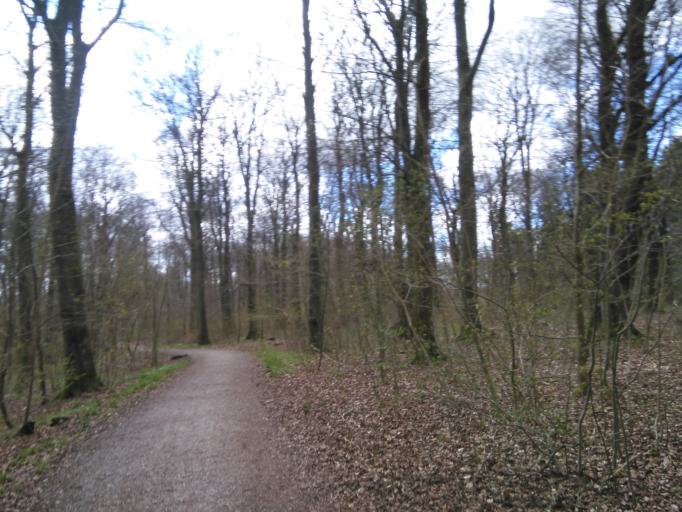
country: DK
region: Central Jutland
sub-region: Arhus Kommune
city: Trige
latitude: 56.2330
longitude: 10.1803
